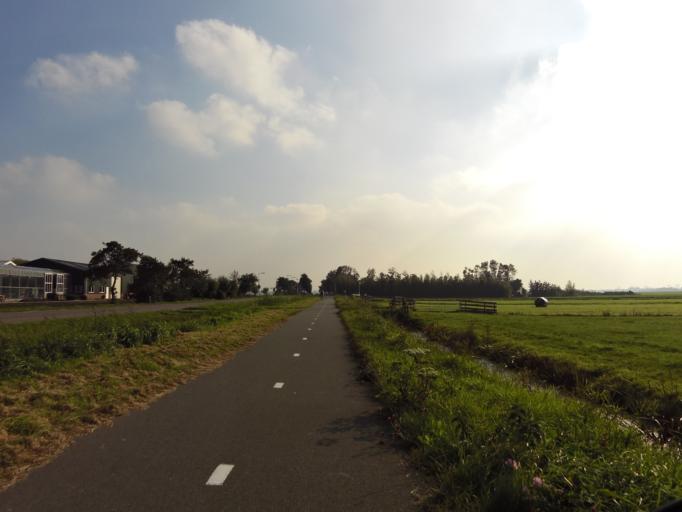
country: NL
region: South Holland
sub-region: Gemeente Rijnwoude
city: Benthuizen
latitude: 52.1063
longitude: 4.5359
